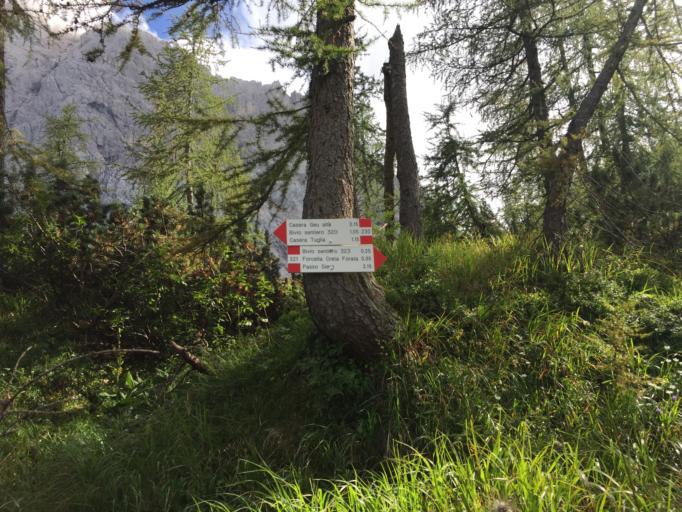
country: IT
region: Veneto
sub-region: Provincia di Belluno
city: Granvilla
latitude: 46.5485
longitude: 12.7338
